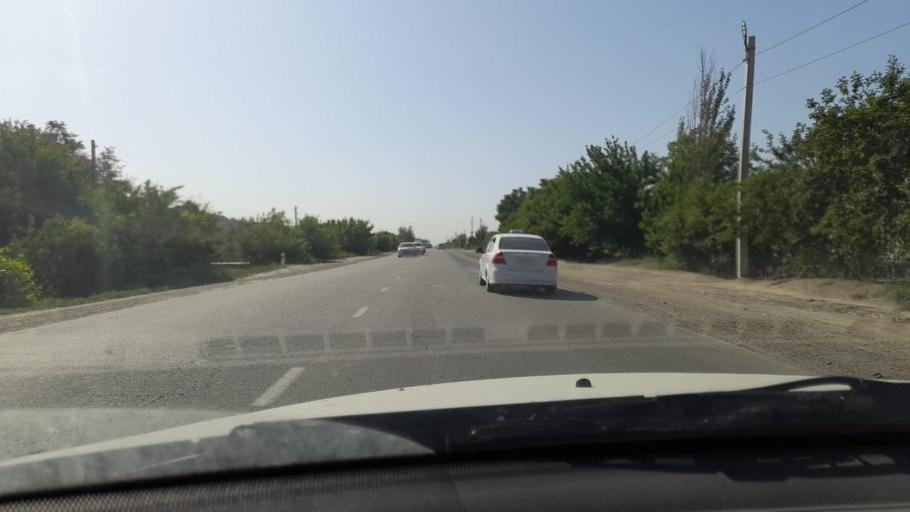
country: UZ
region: Bukhara
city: Romiton
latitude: 39.9069
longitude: 64.3998
